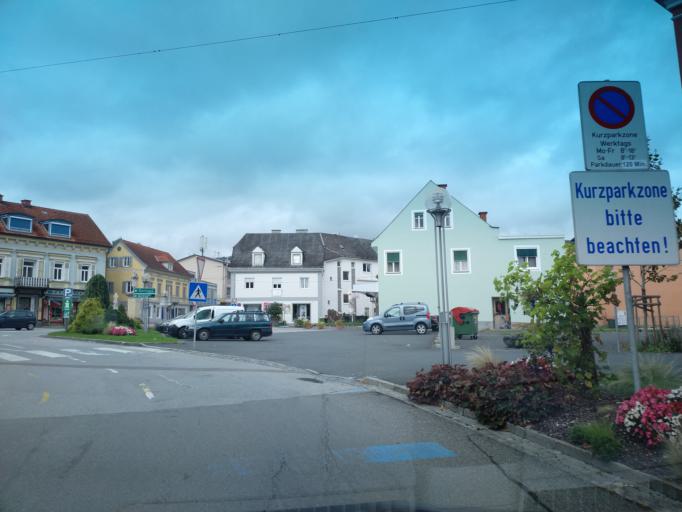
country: AT
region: Styria
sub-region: Politischer Bezirk Deutschlandsberg
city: Deutschlandsberg
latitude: 46.8154
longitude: 15.2168
